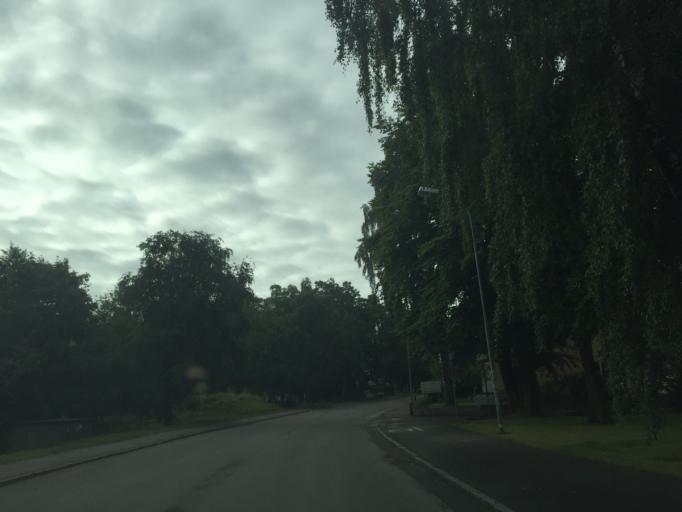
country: SE
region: Skane
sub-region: Angelholms Kommun
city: AEngelholm
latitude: 56.2428
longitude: 12.8565
